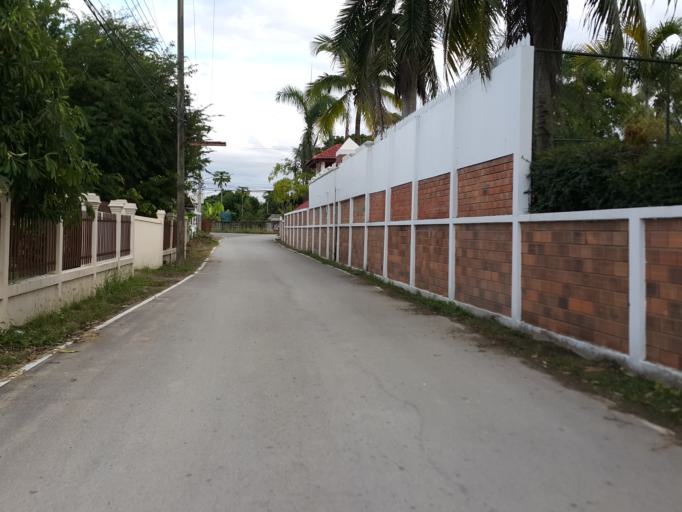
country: TH
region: Chiang Mai
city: San Sai
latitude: 18.8695
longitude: 99.1121
